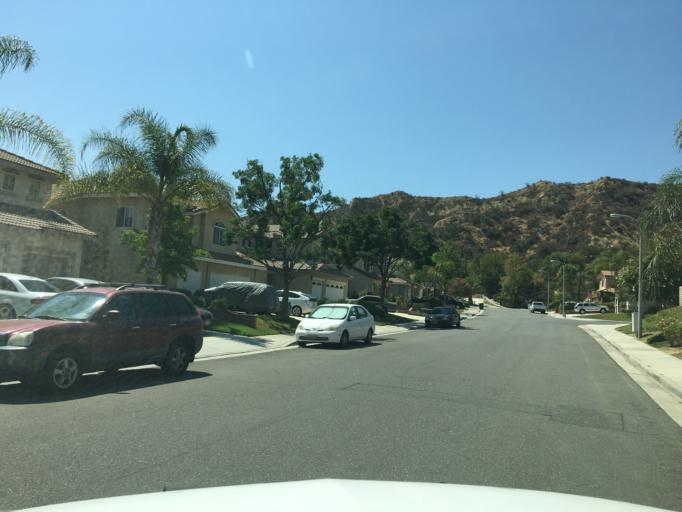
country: US
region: California
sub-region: Los Angeles County
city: Castaic
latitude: 34.4720
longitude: -118.6334
